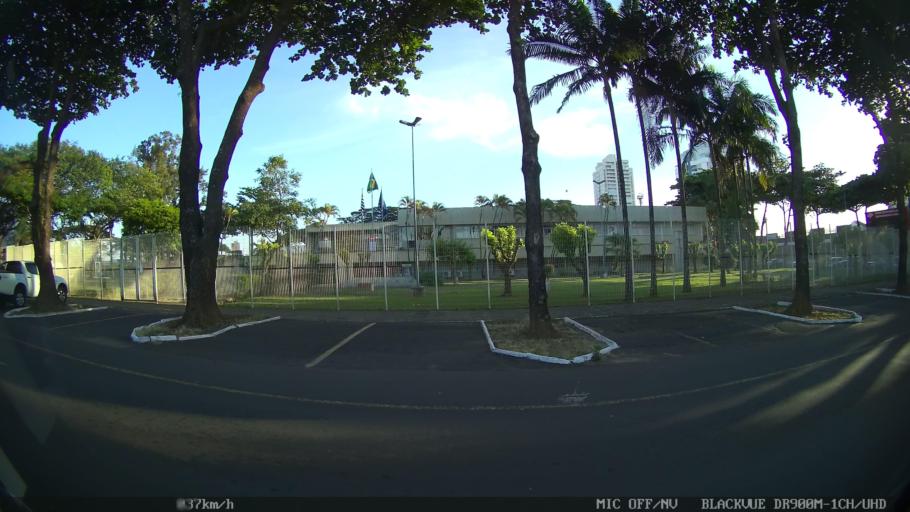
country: BR
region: Sao Paulo
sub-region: Franca
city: Franca
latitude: -20.5277
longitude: -47.3931
